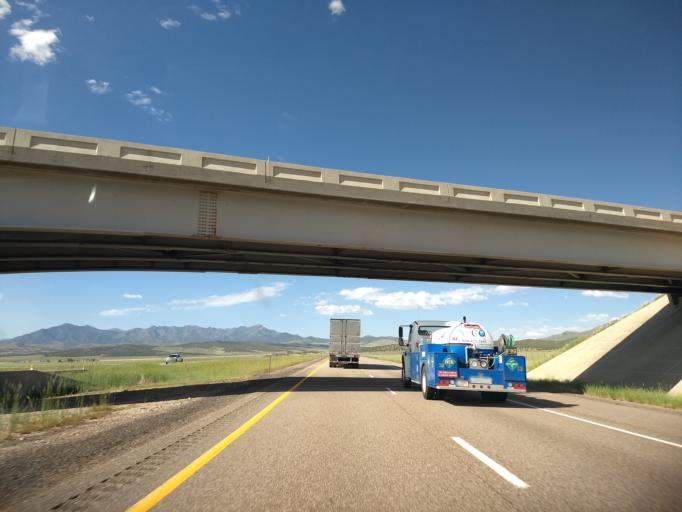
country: US
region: Utah
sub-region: Millard County
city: Fillmore
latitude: 39.1104
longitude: -112.2536
